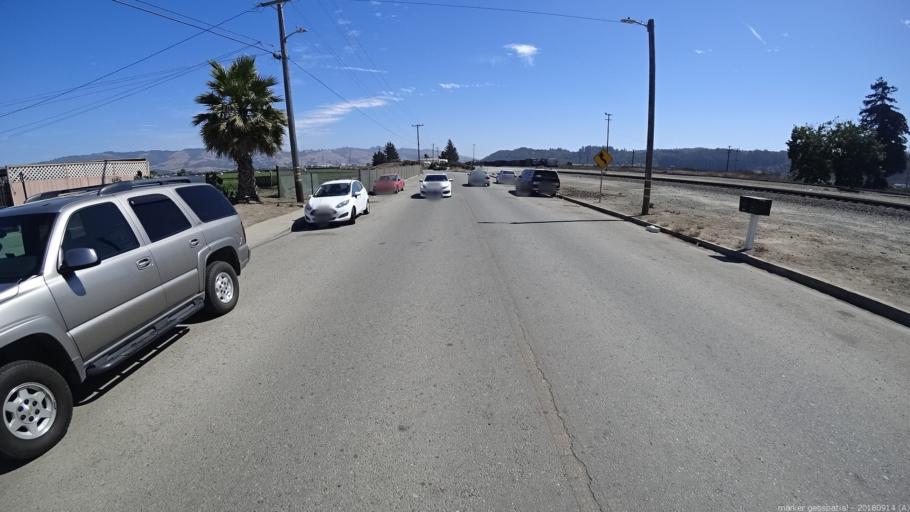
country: US
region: California
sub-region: Monterey County
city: Pajaro
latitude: 36.8970
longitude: -121.7403
